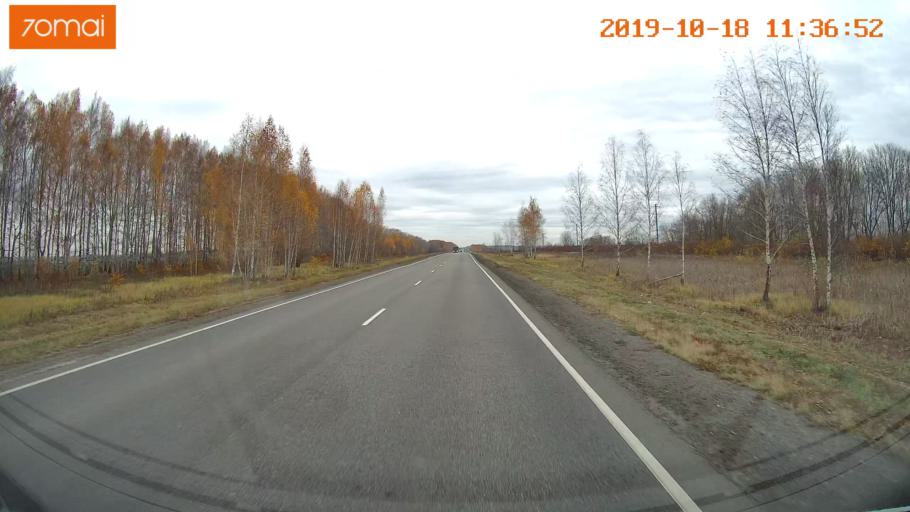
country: RU
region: Rjazan
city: Oktyabr'skiy
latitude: 54.1456
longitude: 38.8171
